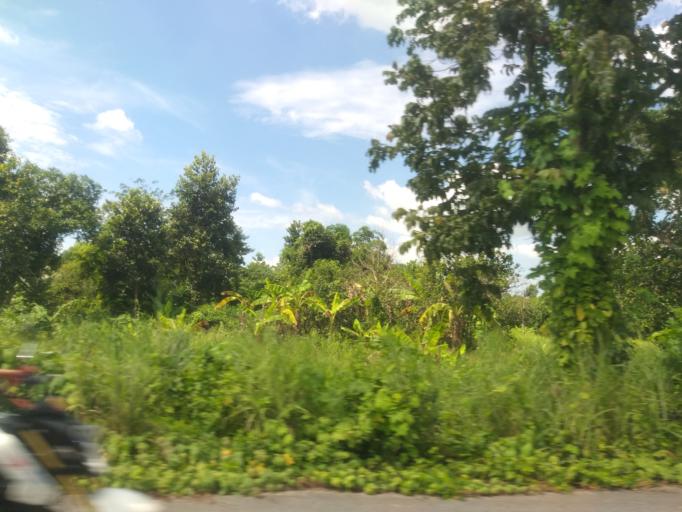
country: TH
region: Nakhon Nayok
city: Nakhon Nayok
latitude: 14.2750
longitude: 101.2765
